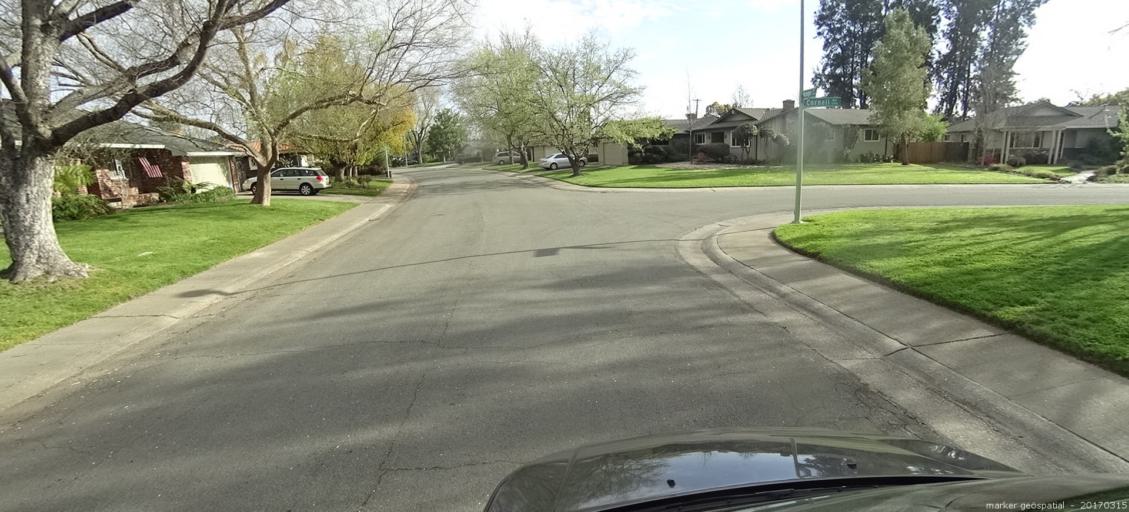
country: US
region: California
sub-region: Sacramento County
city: Parkway
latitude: 38.5064
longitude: -121.5086
